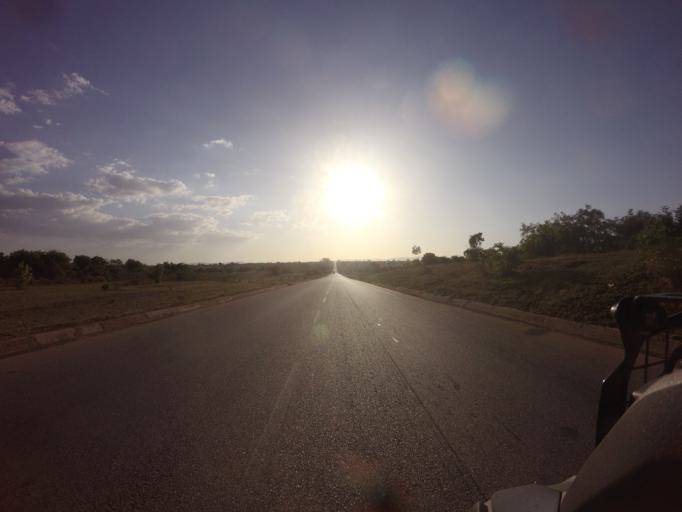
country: AO
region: Huila
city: Lubango
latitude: -14.7956
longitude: 13.6906
